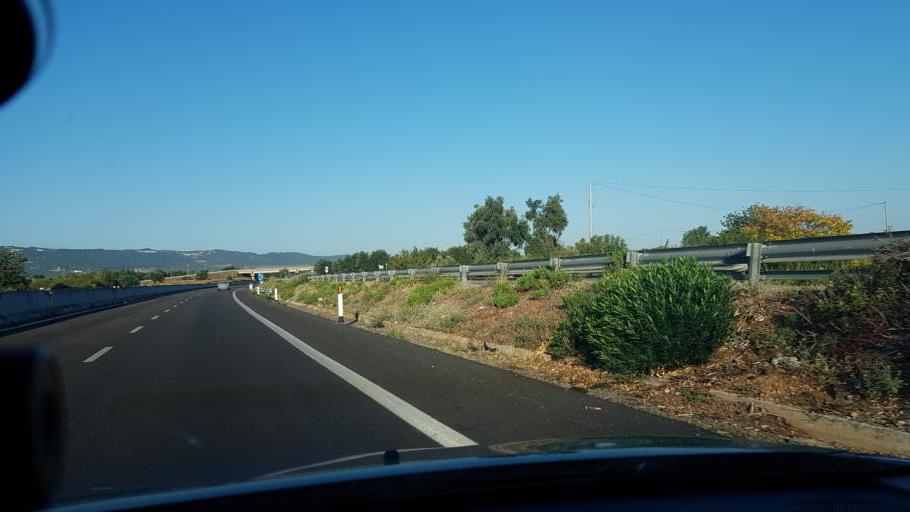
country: IT
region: Apulia
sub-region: Provincia di Brindisi
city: Pezze di Greco
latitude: 40.8341
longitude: 17.3956
